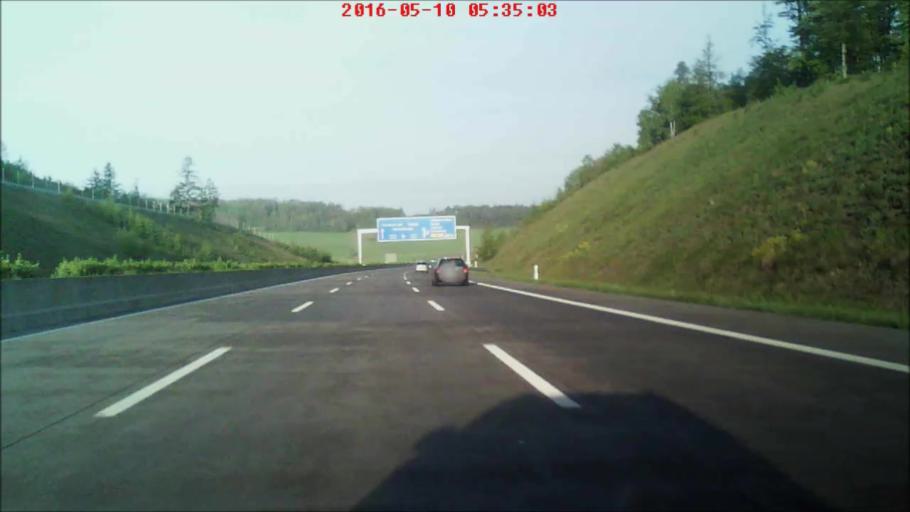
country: DE
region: Thuringia
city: Krauthausen
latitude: 51.0091
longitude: 10.2831
